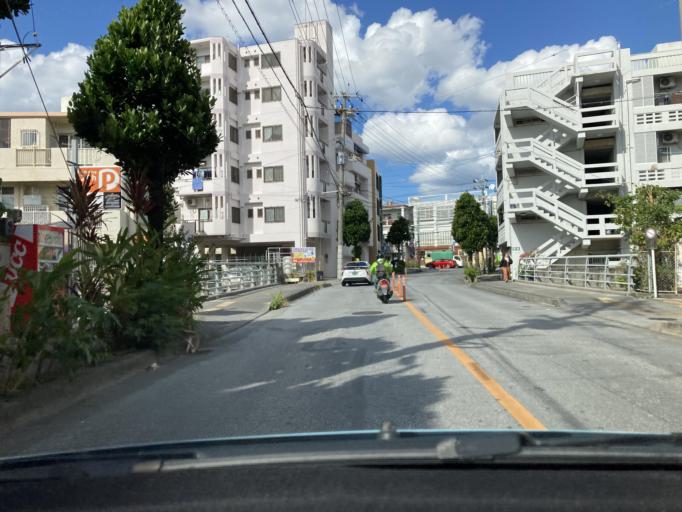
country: JP
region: Okinawa
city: Naha-shi
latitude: 26.2166
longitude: 127.7000
